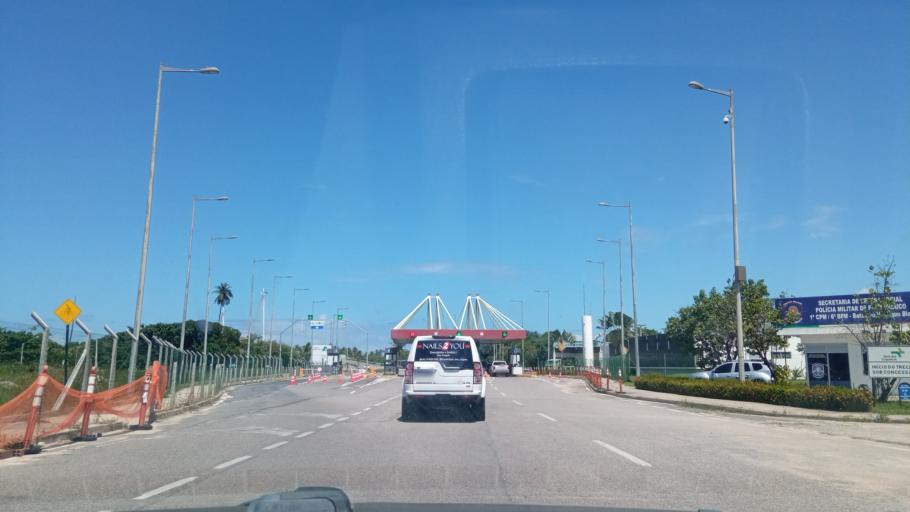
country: BR
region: Pernambuco
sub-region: Jaboatao Dos Guararapes
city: Jaboatao
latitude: -8.2379
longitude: -34.9402
